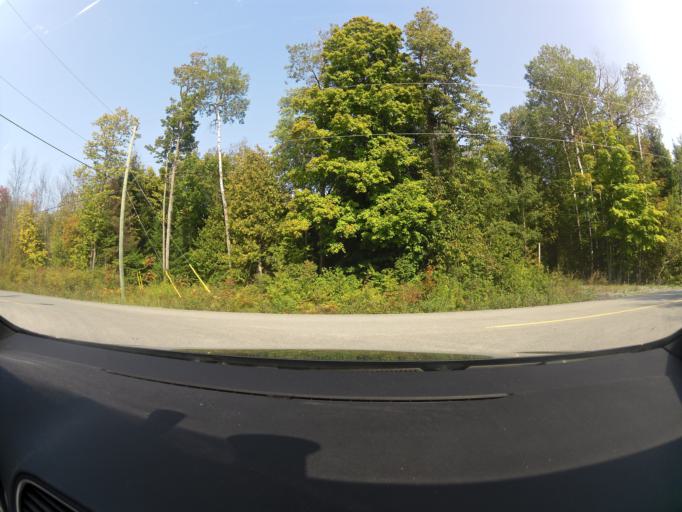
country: CA
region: Ontario
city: Carleton Place
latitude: 45.3302
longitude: -76.1564
